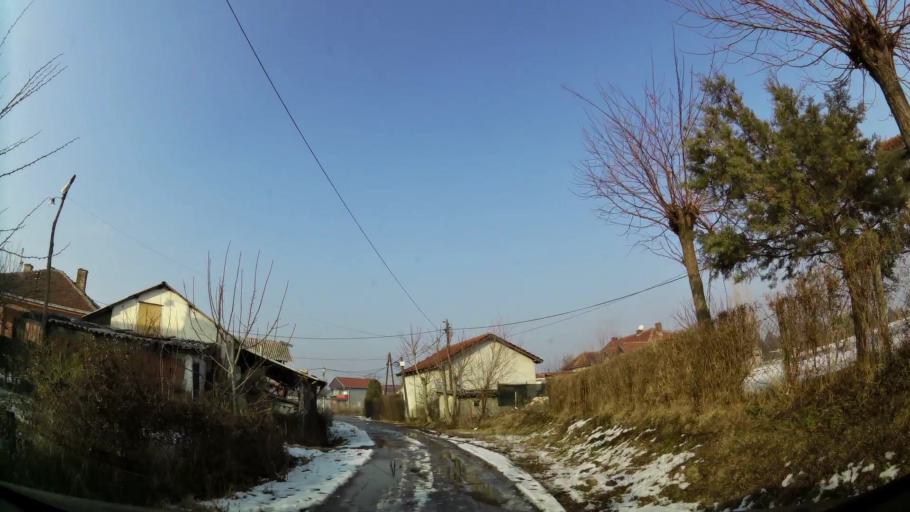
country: MK
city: Kadino
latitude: 41.9546
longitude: 21.6025
